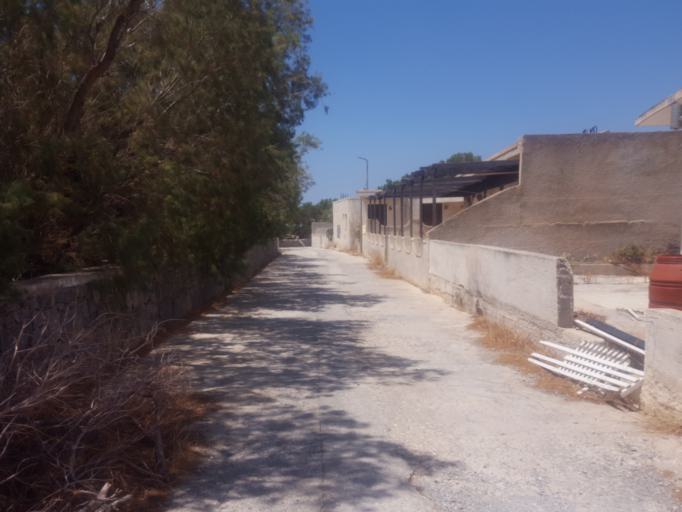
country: GR
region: Crete
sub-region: Nomos Lasithiou
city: Kato Chorio
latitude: 35.0165
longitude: 25.8468
